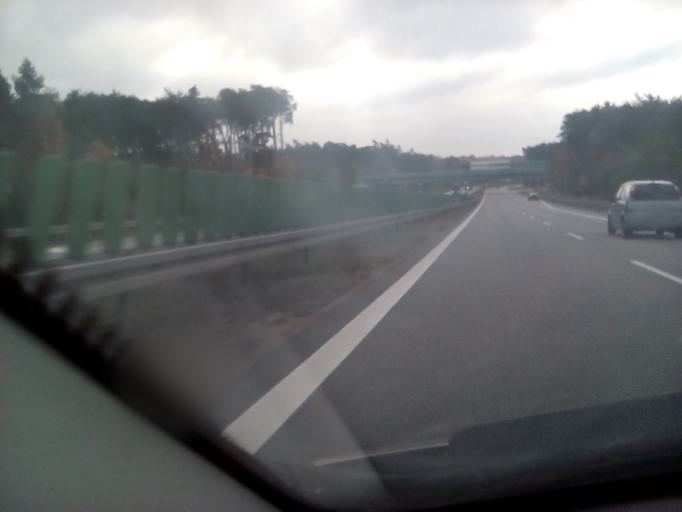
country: PL
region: Masovian Voivodeship
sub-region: Powiat bialobrzeski
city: Bialobrzegi
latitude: 51.6517
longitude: 20.9701
